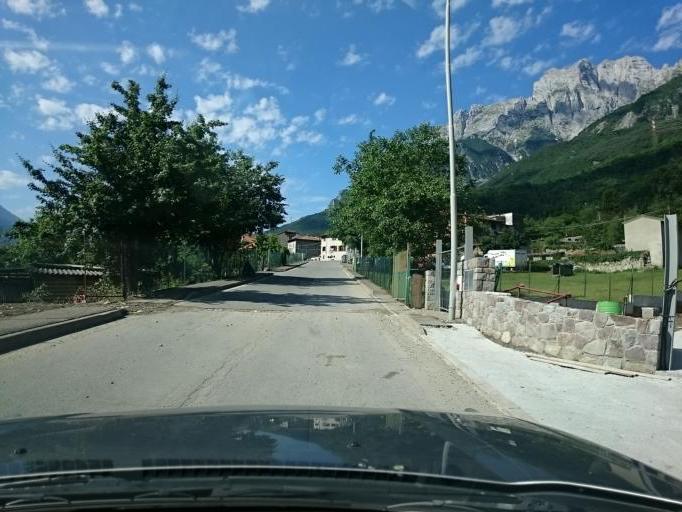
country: IT
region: Lombardy
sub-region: Provincia di Brescia
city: Capo di Ponte
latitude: 46.0300
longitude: 10.3361
